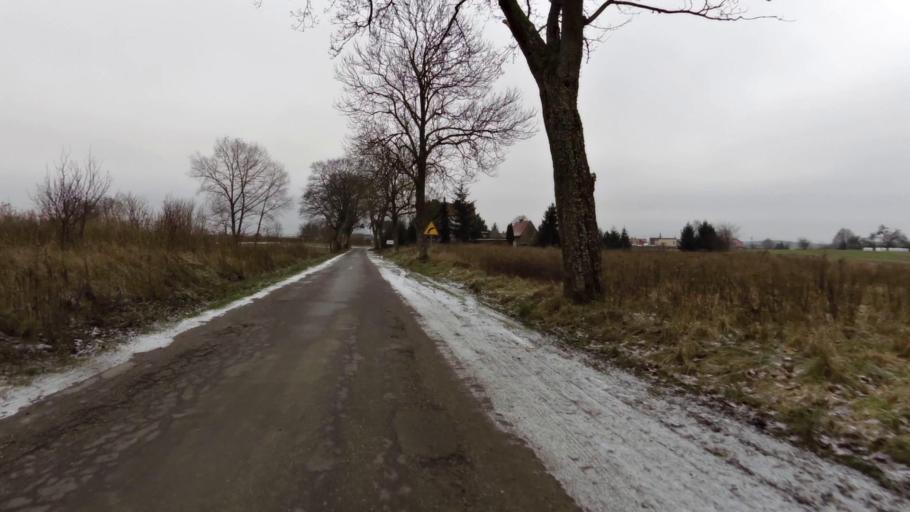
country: PL
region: West Pomeranian Voivodeship
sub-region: Powiat szczecinecki
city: Szczecinek
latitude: 53.6535
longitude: 16.6340
